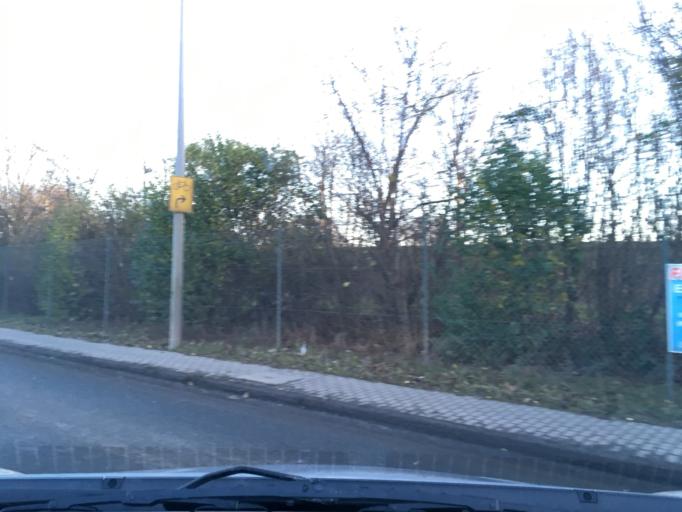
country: DE
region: Lower Saxony
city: Uelzen
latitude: 52.9812
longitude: 10.5629
